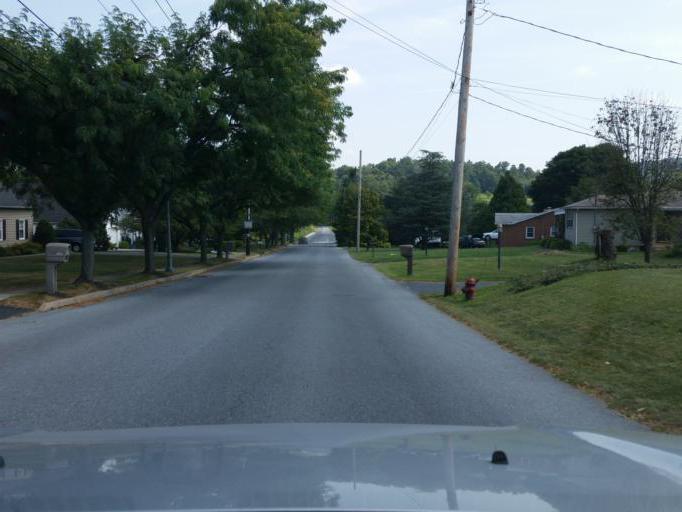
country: US
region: Pennsylvania
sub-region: Dauphin County
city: Hummelstown
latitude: 40.2392
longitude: -76.7142
